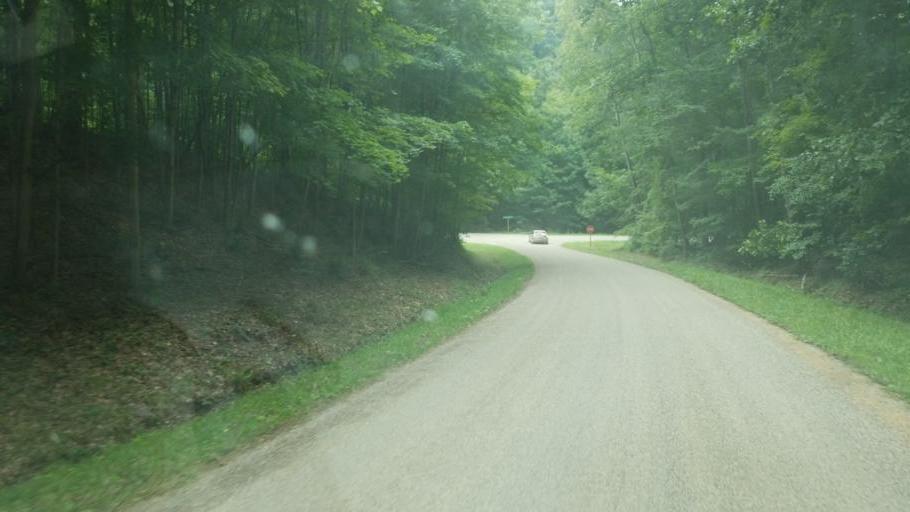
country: US
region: Ohio
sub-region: Knox County
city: Danville
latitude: 40.4479
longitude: -82.3335
